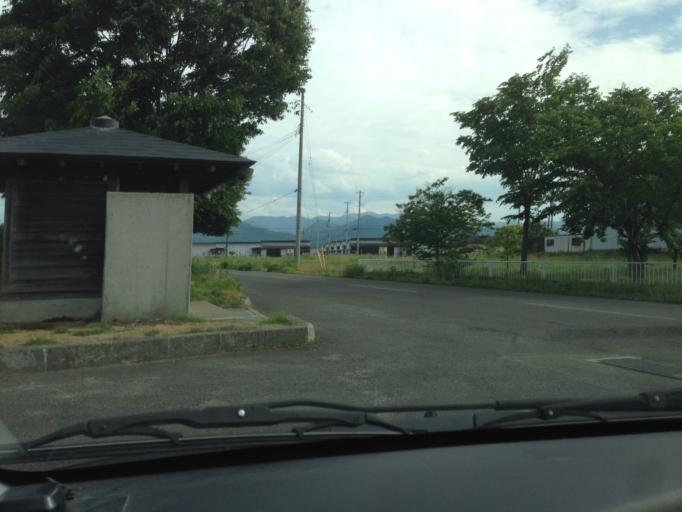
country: JP
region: Fukushima
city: Kitakata
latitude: 37.4695
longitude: 139.8603
